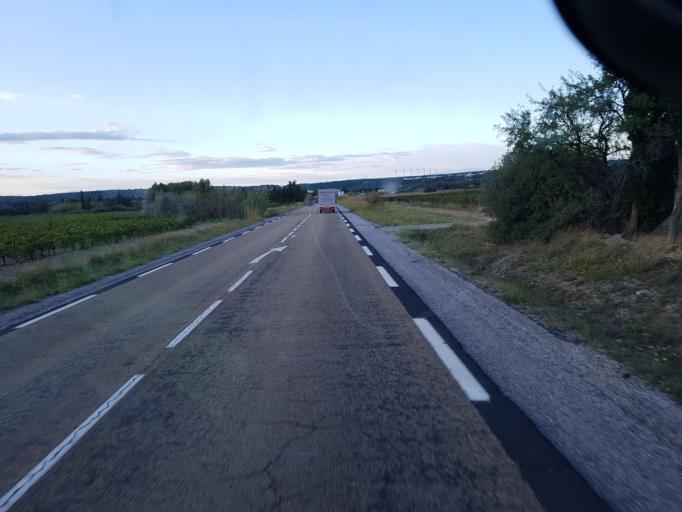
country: FR
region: Languedoc-Roussillon
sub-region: Departement de l'Aude
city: Leucate
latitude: 42.9533
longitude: 2.9862
